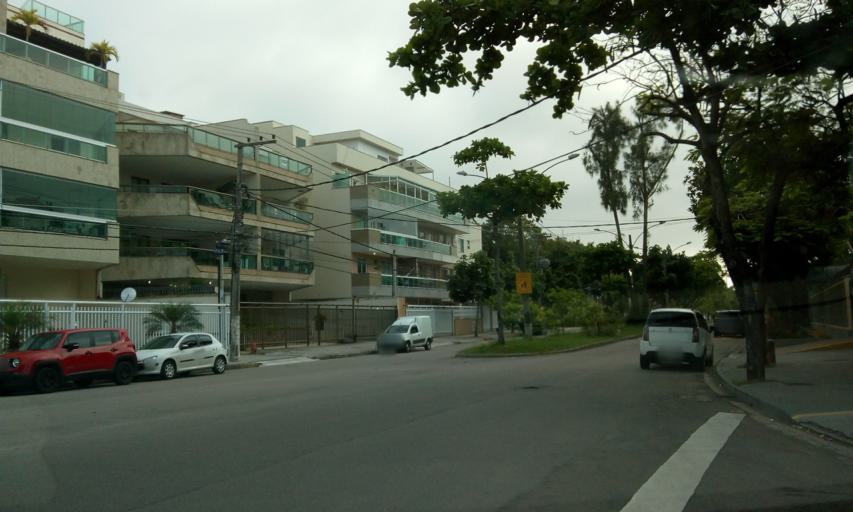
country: BR
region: Rio de Janeiro
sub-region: Nilopolis
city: Nilopolis
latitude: -23.0141
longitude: -43.4488
